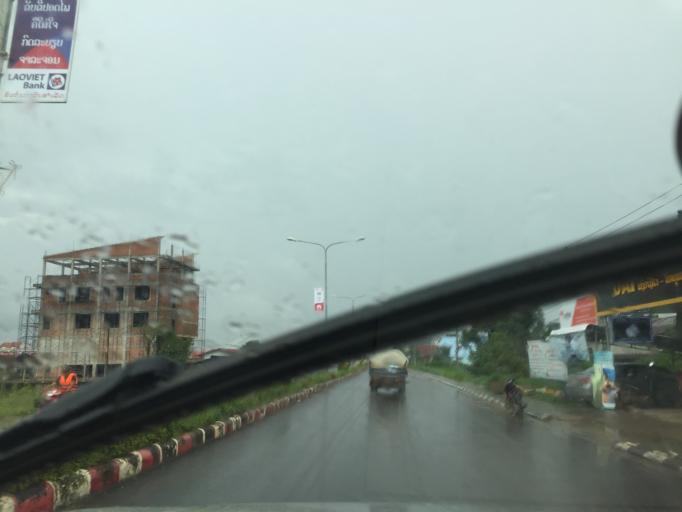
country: LA
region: Attapu
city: Attapu
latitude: 14.8183
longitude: 106.8166
